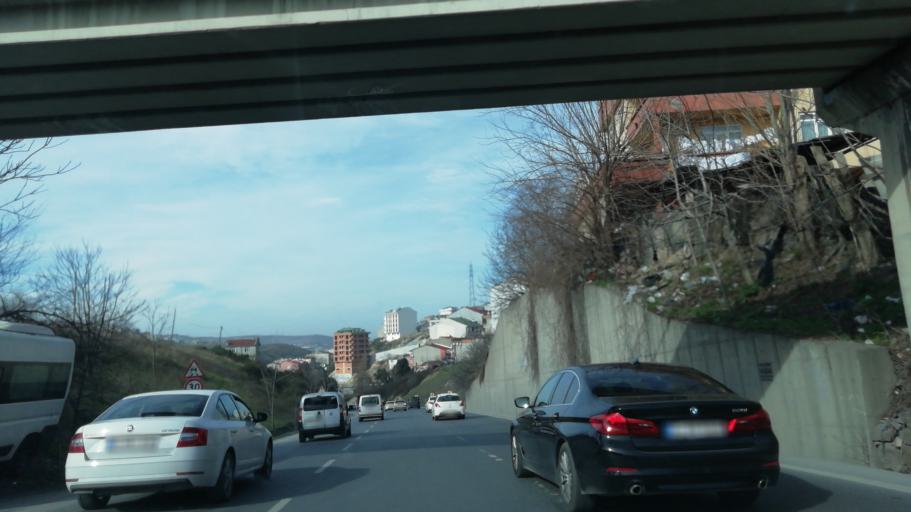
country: TR
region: Istanbul
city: Basaksehir
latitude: 41.0626
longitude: 28.7520
